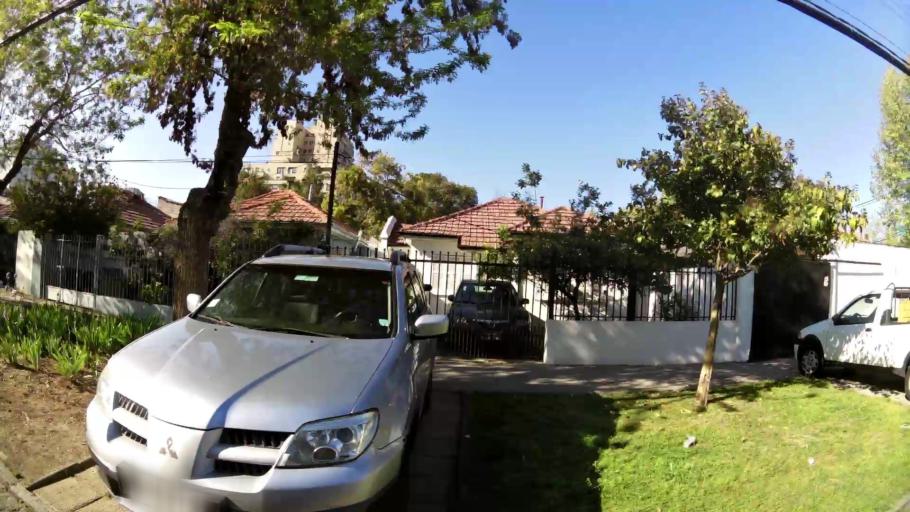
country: CL
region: Santiago Metropolitan
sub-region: Provincia de Santiago
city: Villa Presidente Frei, Nunoa, Santiago, Chile
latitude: -33.4531
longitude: -70.5799
